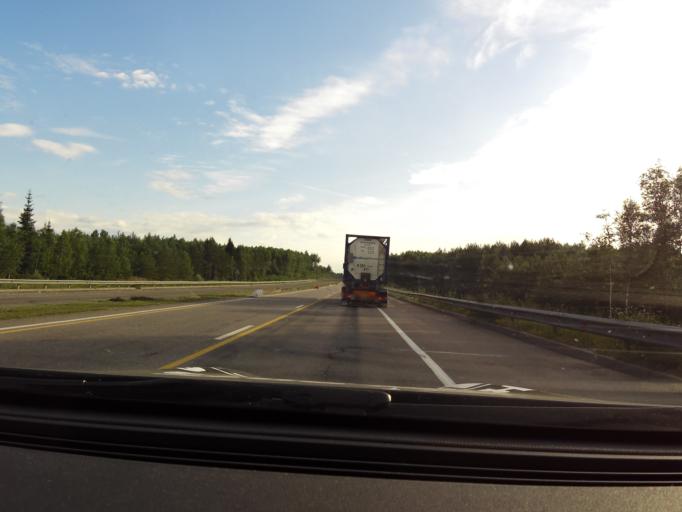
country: RU
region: Vladimir
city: Sudogda
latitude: 56.1232
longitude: 40.8615
